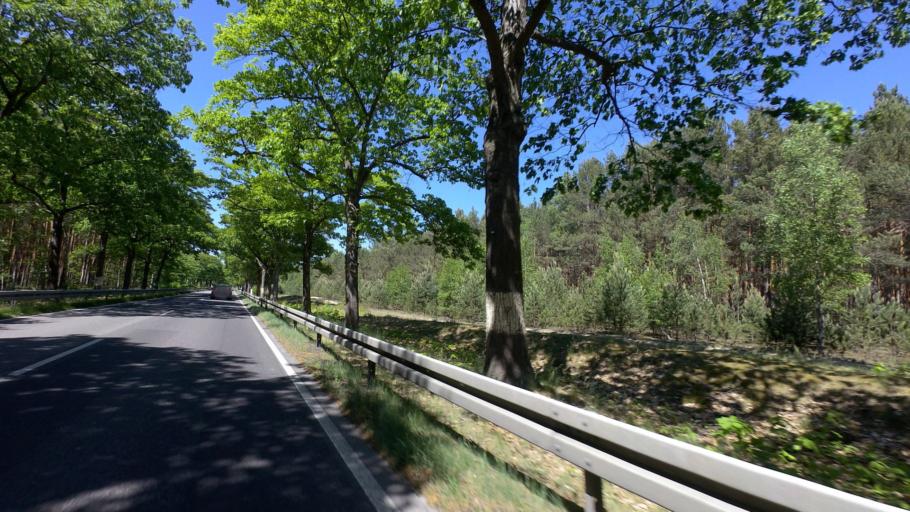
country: DE
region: Brandenburg
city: Drehnow
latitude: 51.8938
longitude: 14.3665
